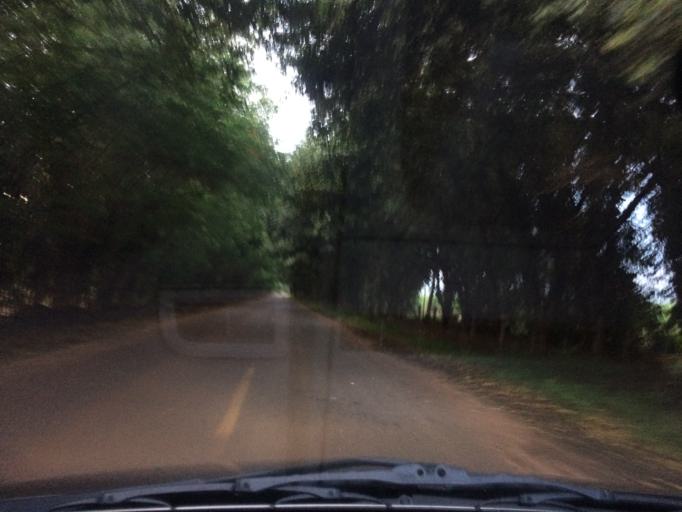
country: BR
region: Sao Paulo
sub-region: Tambau
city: Tambau
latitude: -21.7341
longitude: -47.1792
